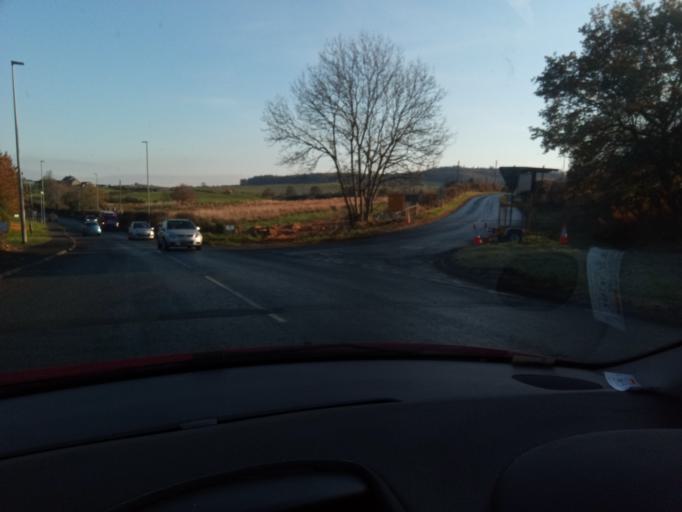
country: GB
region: Scotland
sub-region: The Scottish Borders
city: Hawick
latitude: 55.4353
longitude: -2.7528
